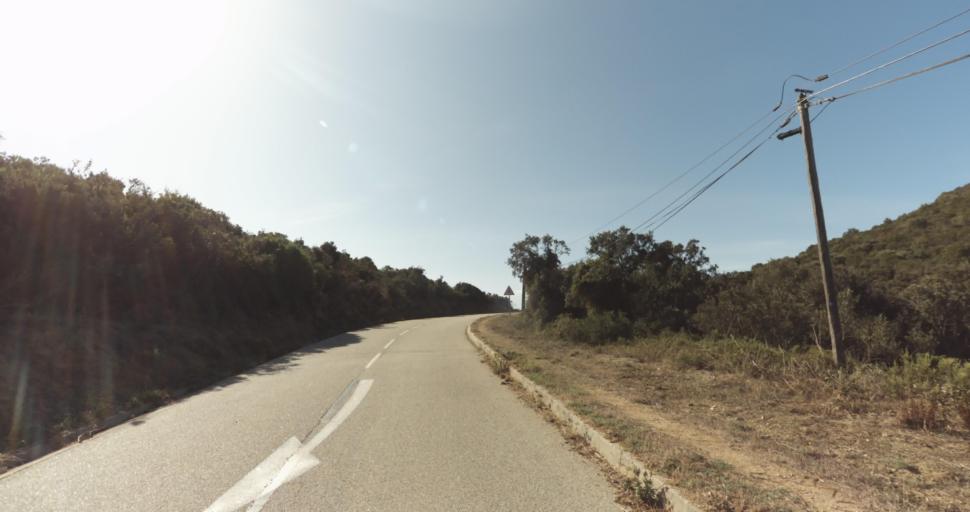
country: FR
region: Corsica
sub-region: Departement de la Corse-du-Sud
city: Ajaccio
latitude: 41.9226
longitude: 8.6426
